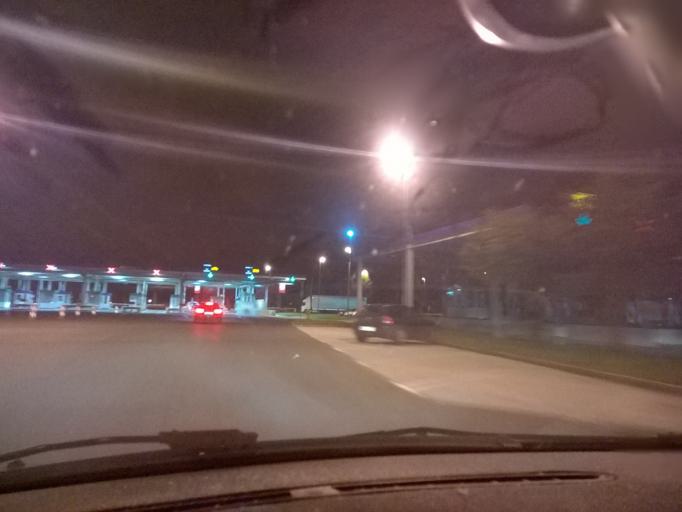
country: SI
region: Zetale
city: Zetale
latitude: 46.2765
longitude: 15.8648
